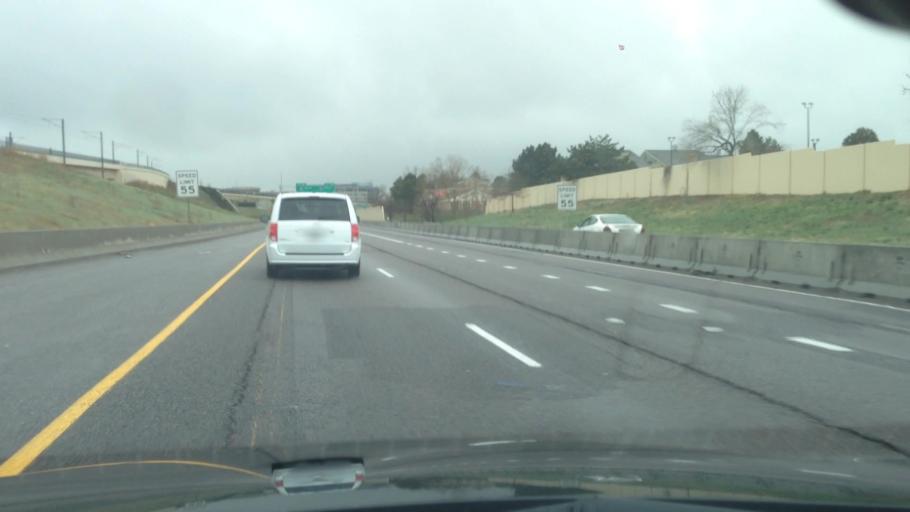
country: US
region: Colorado
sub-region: Arapahoe County
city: Castlewood
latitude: 39.6354
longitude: -104.8997
